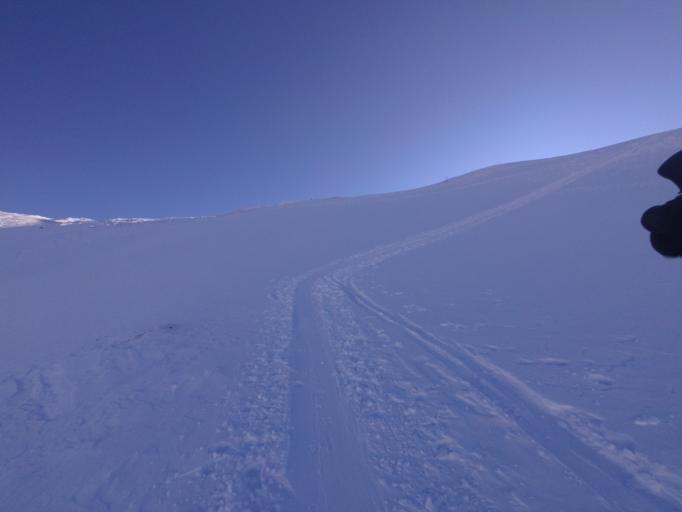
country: AT
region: Salzburg
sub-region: Politischer Bezirk Sankt Johann im Pongau
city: Huttschlag
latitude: 47.1747
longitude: 13.3032
